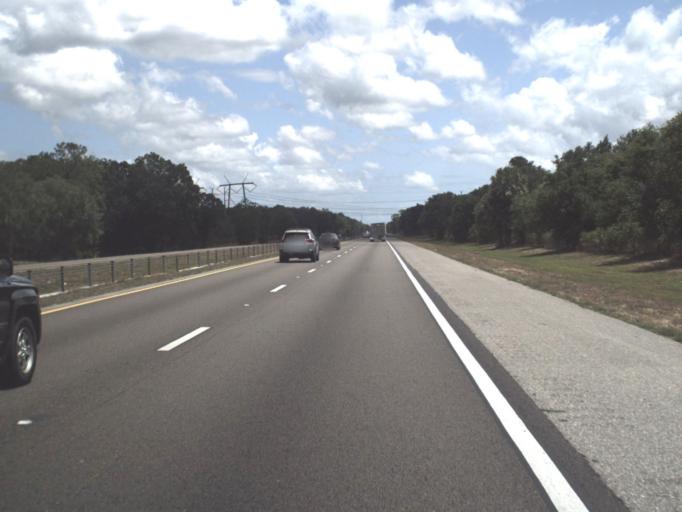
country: US
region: Florida
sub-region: Orange County
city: Wedgefield
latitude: 28.4523
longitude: -81.0172
